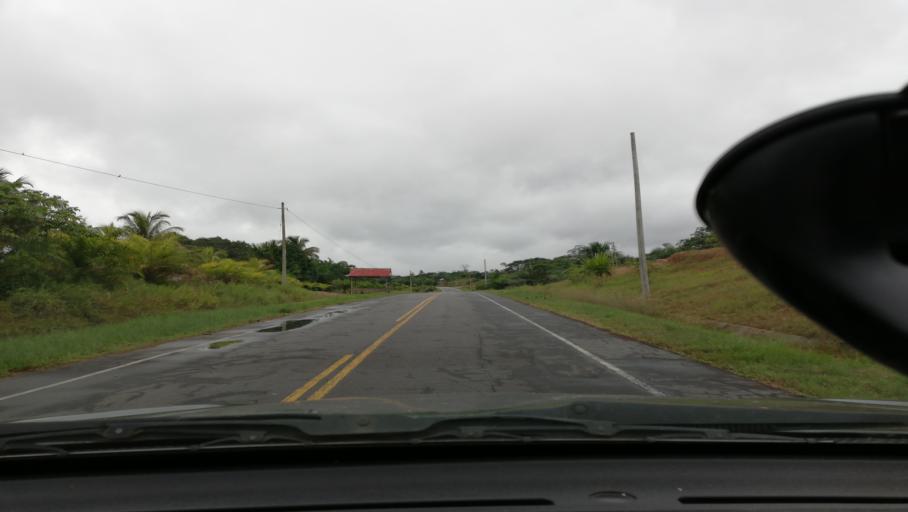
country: PE
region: Loreto
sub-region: Provincia de Loreto
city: Nauta
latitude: -4.3466
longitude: -73.5422
